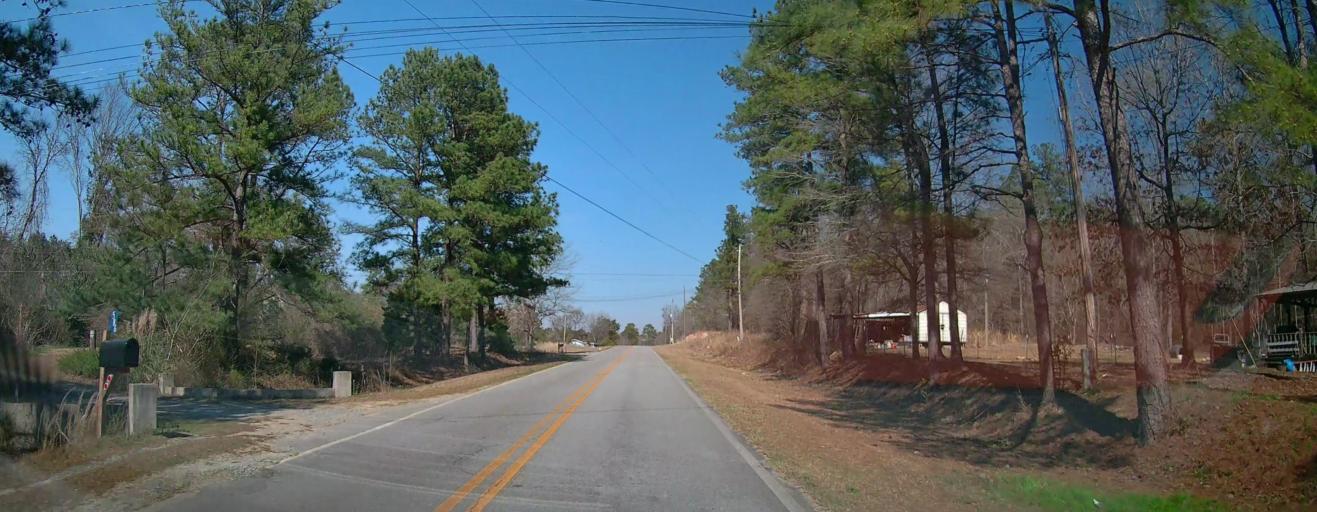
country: US
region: Georgia
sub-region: Bibb County
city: Macon
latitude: 32.8962
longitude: -83.5416
